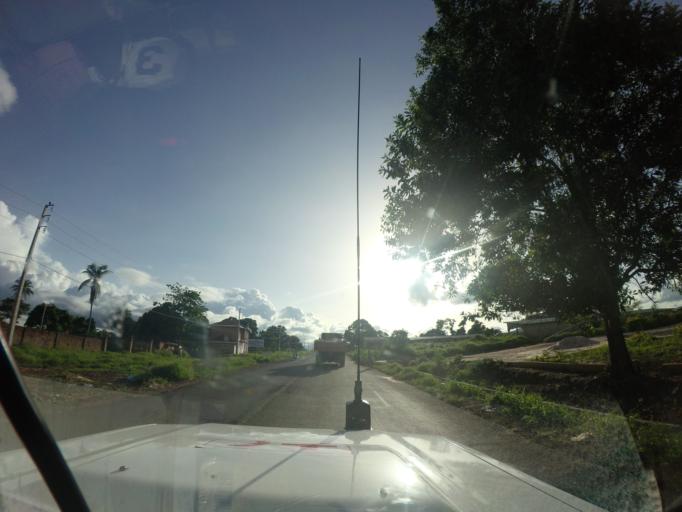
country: GN
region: Kindia
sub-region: Kindia
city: Kindia
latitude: 10.0323
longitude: -12.8552
